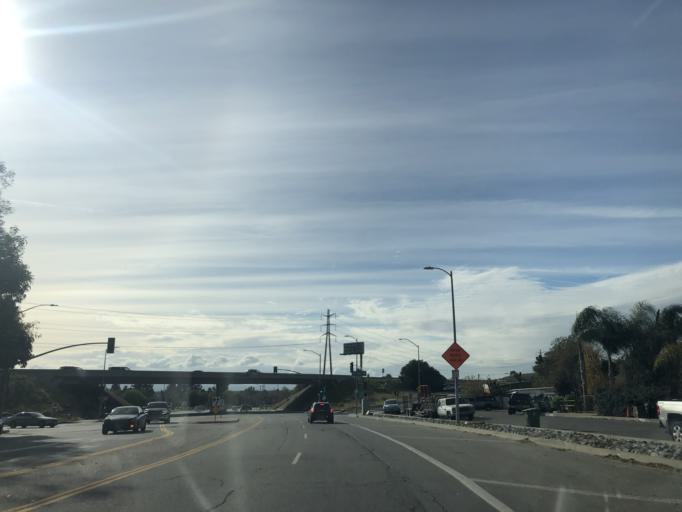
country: US
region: California
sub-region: Los Angeles County
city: San Fernando
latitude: 34.2758
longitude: -118.3795
